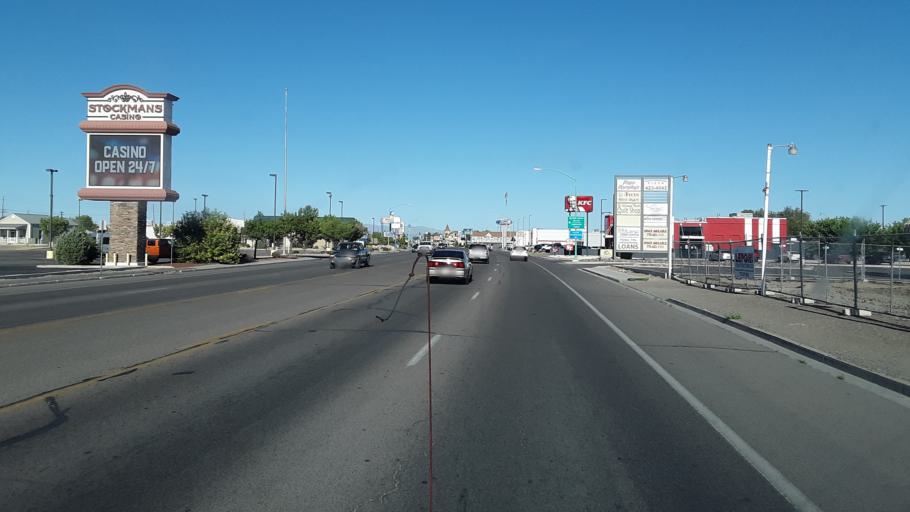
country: US
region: Nevada
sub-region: Churchill County
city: Fallon
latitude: 39.4750
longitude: -118.7951
